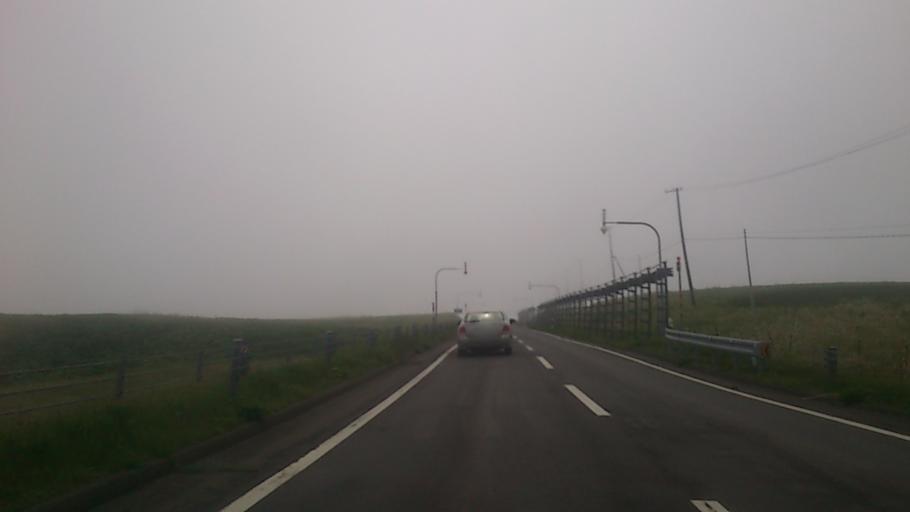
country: JP
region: Hokkaido
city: Nemuro
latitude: 43.1668
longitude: 145.2722
